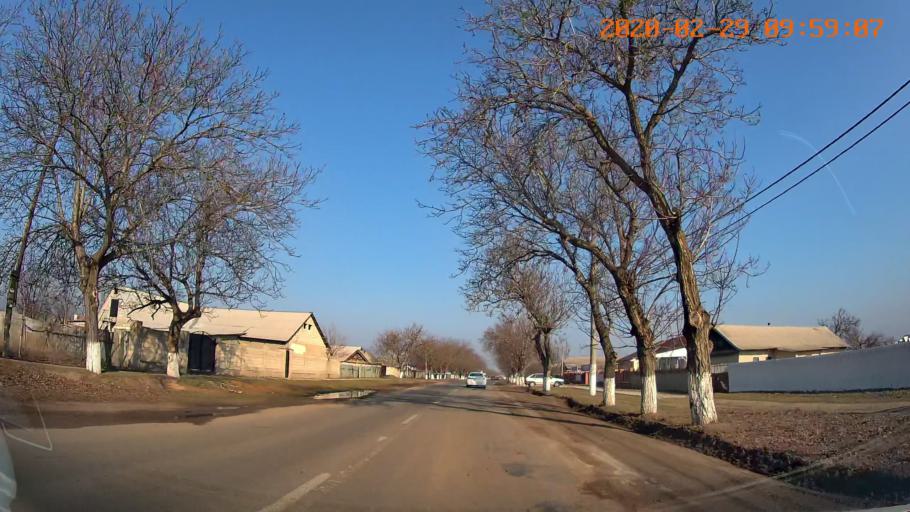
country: MD
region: Telenesti
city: Slobozia
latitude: 46.7541
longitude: 29.6890
